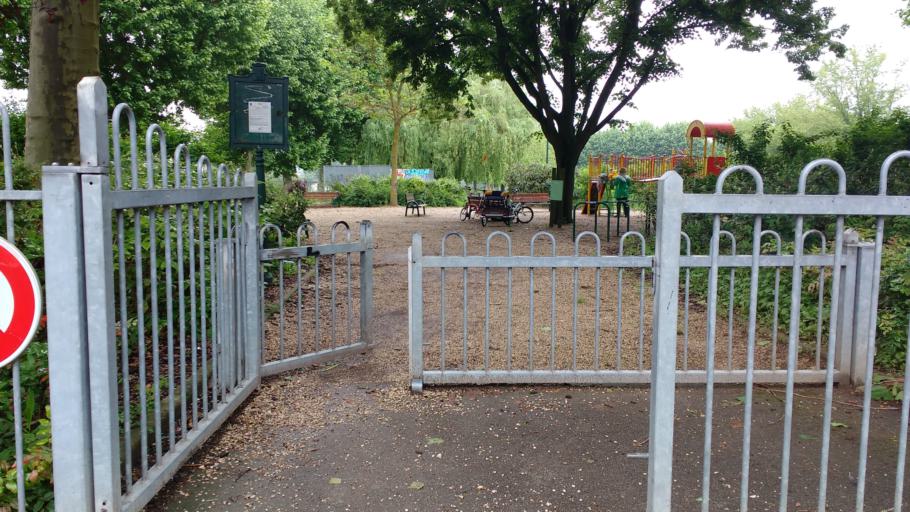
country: FR
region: Bourgogne
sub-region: Departement de l'Yonne
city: Sens
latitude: 48.1990
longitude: 3.2771
